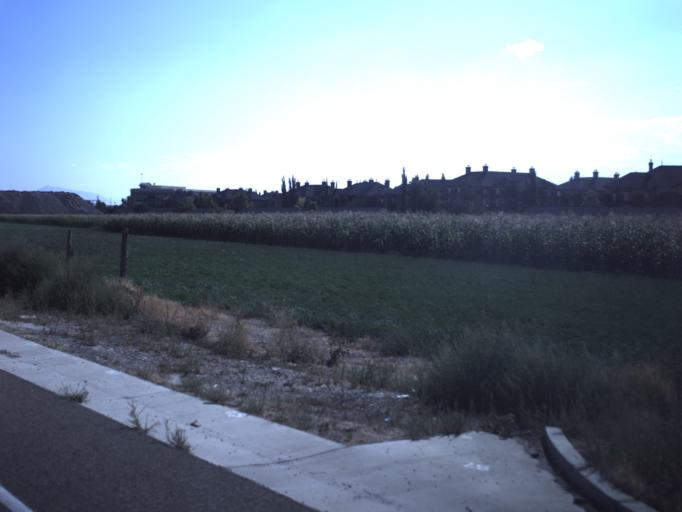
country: US
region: Utah
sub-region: Utah County
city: Pleasant Grove
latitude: 40.3595
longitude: -111.7685
